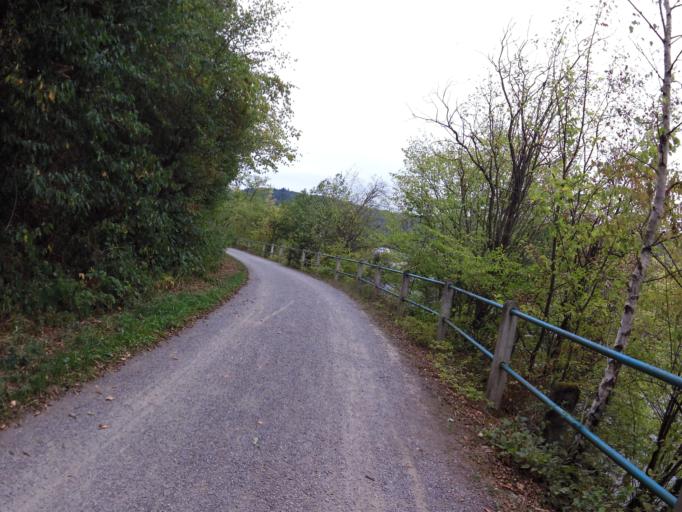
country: DE
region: North Rhine-Westphalia
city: Heimbach
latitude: 50.6099
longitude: 6.3908
